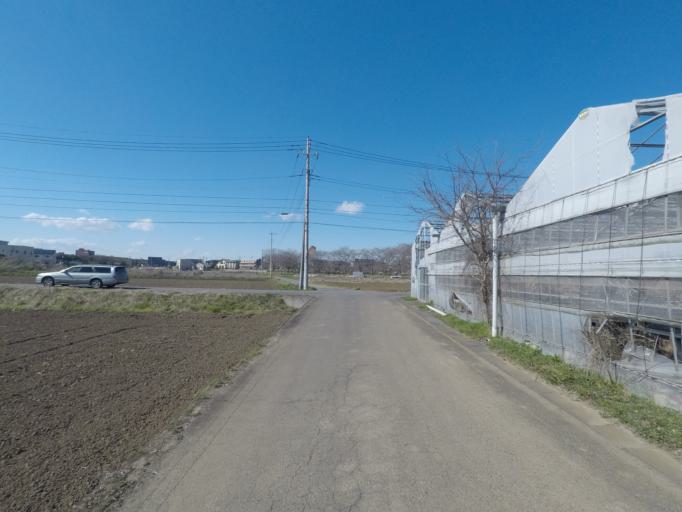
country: JP
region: Ibaraki
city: Naka
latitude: 36.1071
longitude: 140.1125
